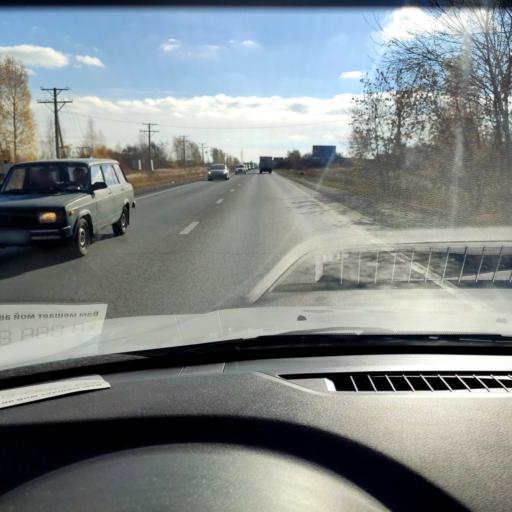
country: RU
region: Samara
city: Tol'yatti
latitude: 53.5511
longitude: 49.3717
